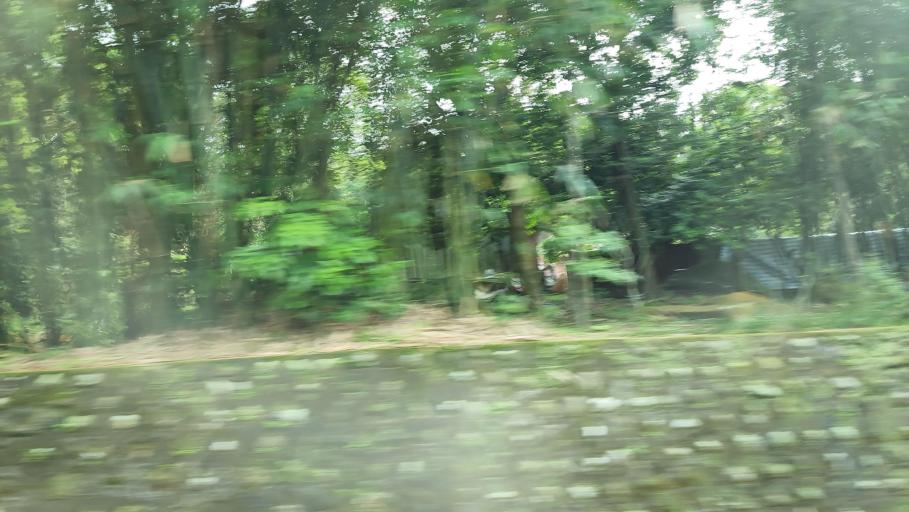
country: TW
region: Taiwan
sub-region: Keelung
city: Keelung
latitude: 25.1487
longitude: 121.6213
